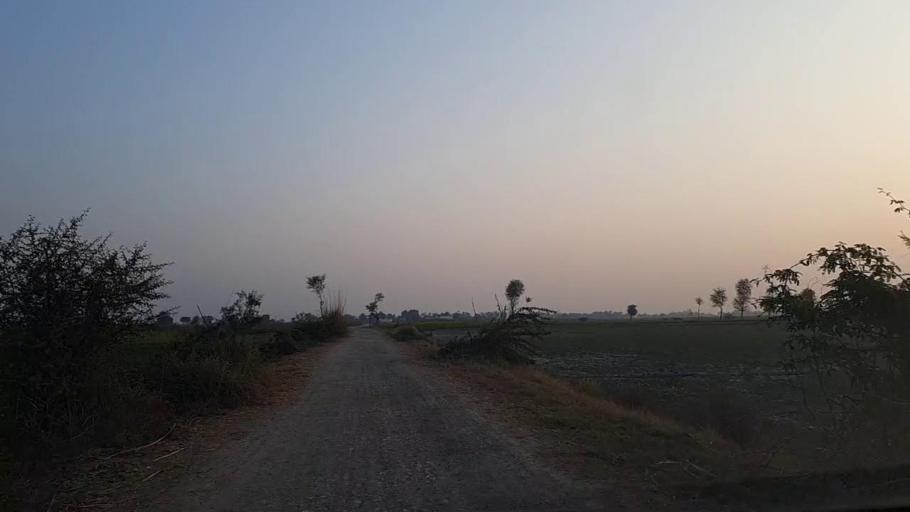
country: PK
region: Sindh
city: Daur
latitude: 26.4393
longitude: 68.3489
